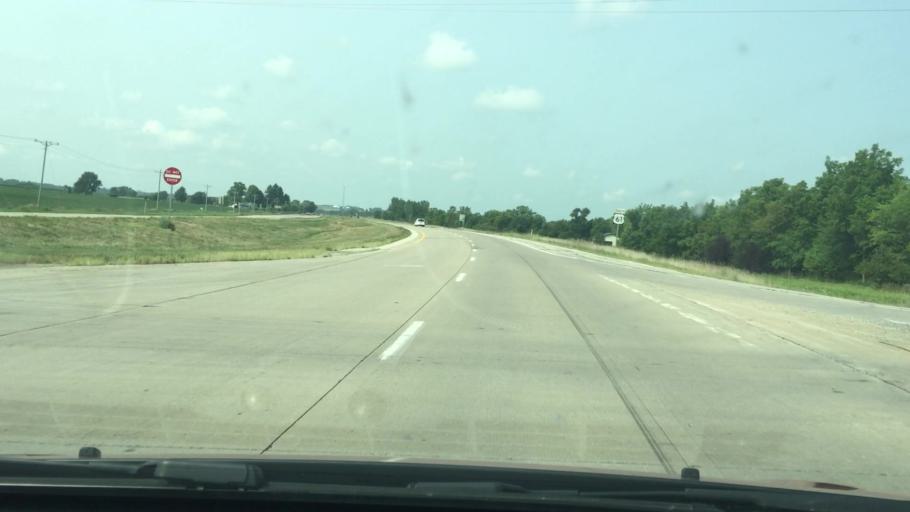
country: US
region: Iowa
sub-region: Cedar County
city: Durant
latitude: 41.5174
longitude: -90.9008
